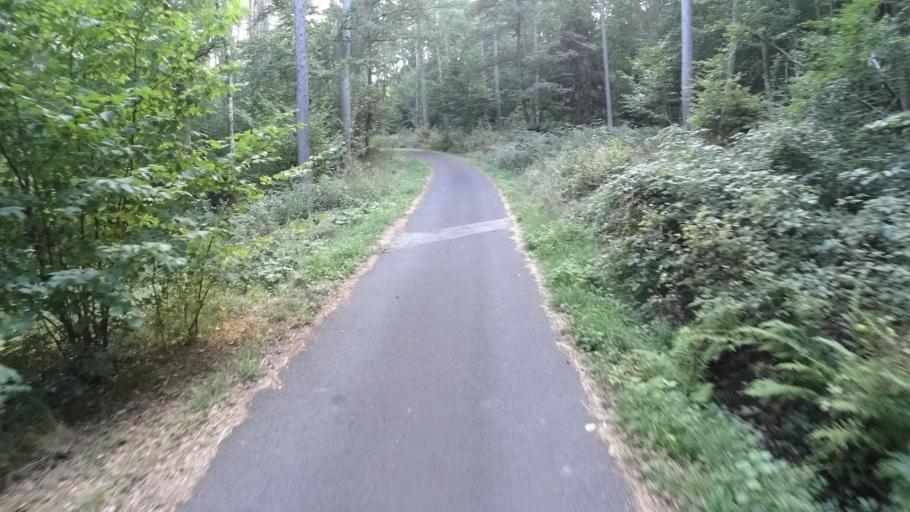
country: DE
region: Rheinland-Pfalz
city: Dichtelbach
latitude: 49.9888
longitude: 7.6908
